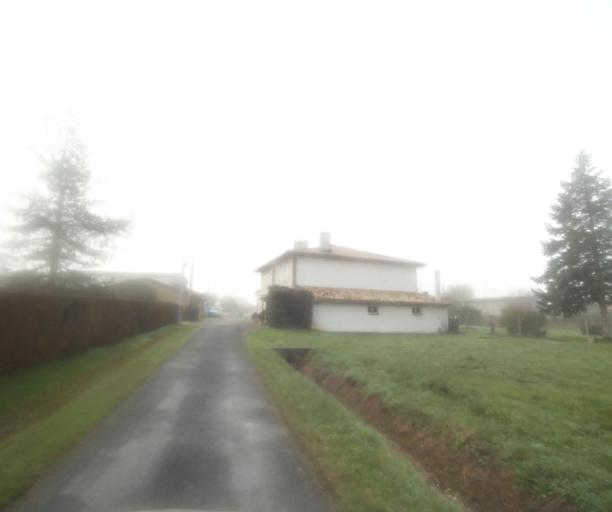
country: FR
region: Midi-Pyrenees
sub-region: Departement de la Haute-Garonne
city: Villaudric
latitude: 43.8172
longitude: 1.4580
